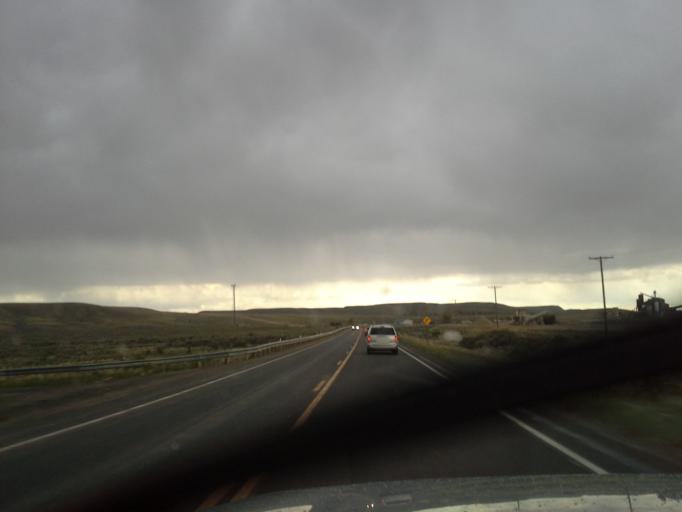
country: US
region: Wyoming
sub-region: Park County
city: Powell
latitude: 45.0630
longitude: -108.6636
